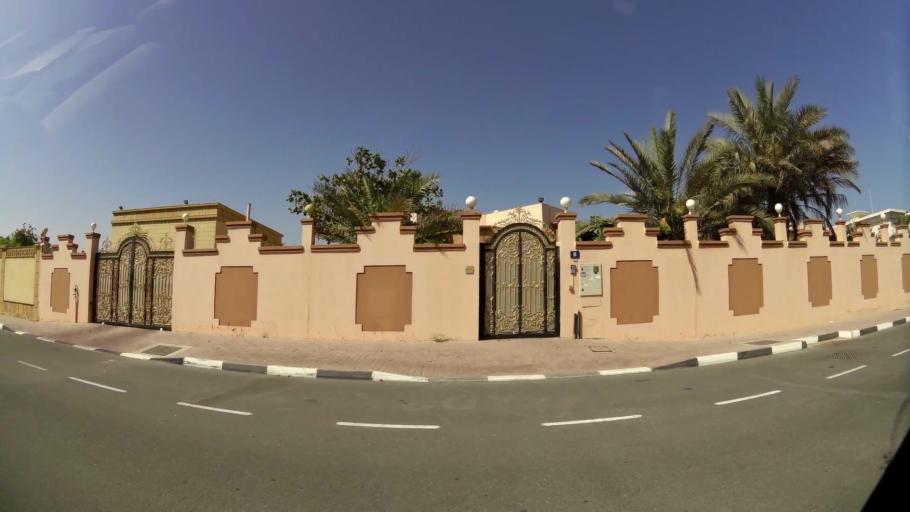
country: AE
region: Ash Shariqah
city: Sharjah
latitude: 25.2479
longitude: 55.2818
